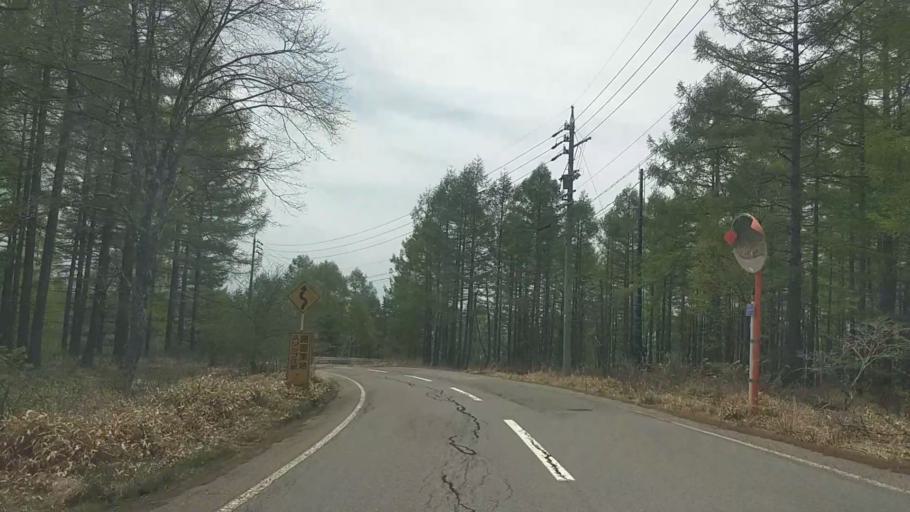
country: JP
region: Nagano
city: Chino
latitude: 36.0469
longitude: 138.3089
